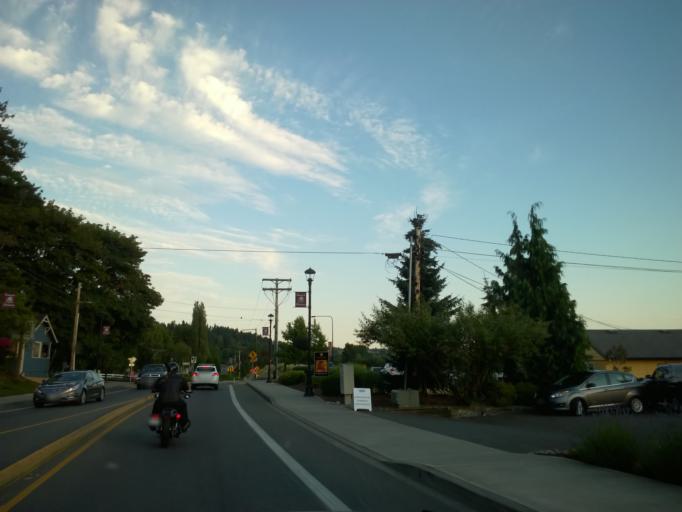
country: US
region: Washington
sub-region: King County
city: Woodinville
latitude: 47.7315
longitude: -122.1407
